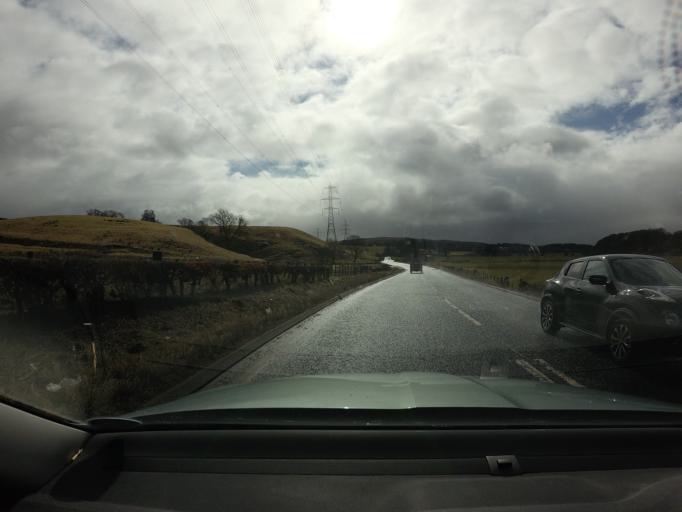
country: GB
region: Scotland
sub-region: South Lanarkshire
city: Douglas
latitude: 55.5881
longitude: -3.8018
